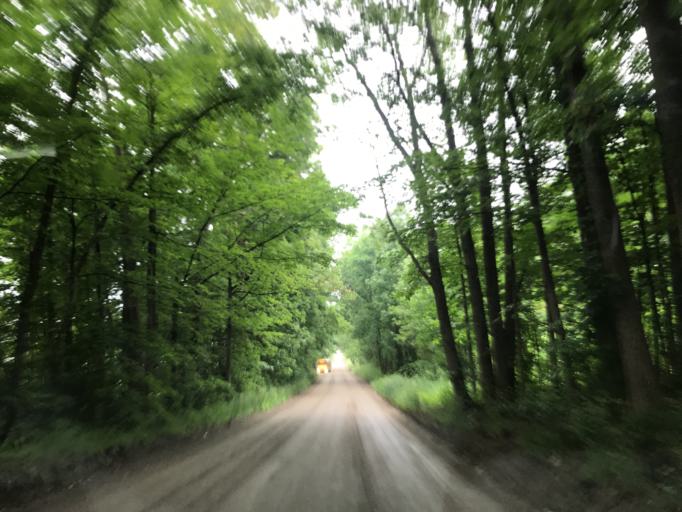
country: US
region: Michigan
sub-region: Oakland County
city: Wixom
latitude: 42.4962
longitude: -83.5949
